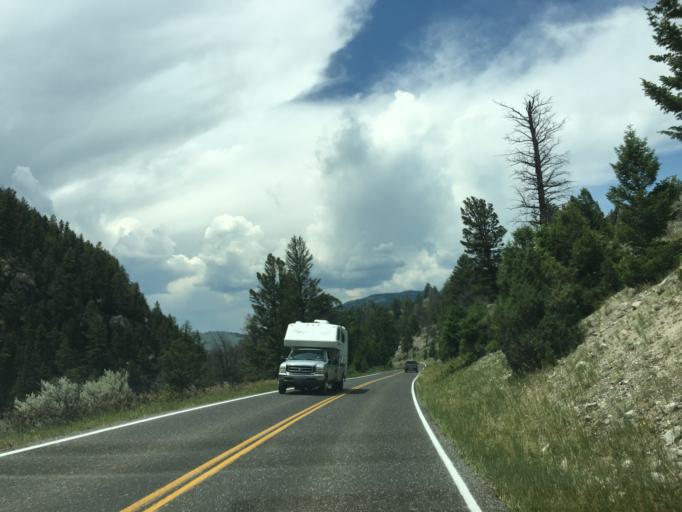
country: US
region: Montana
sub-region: Park County
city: Livingston
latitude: 44.9175
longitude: -110.2917
